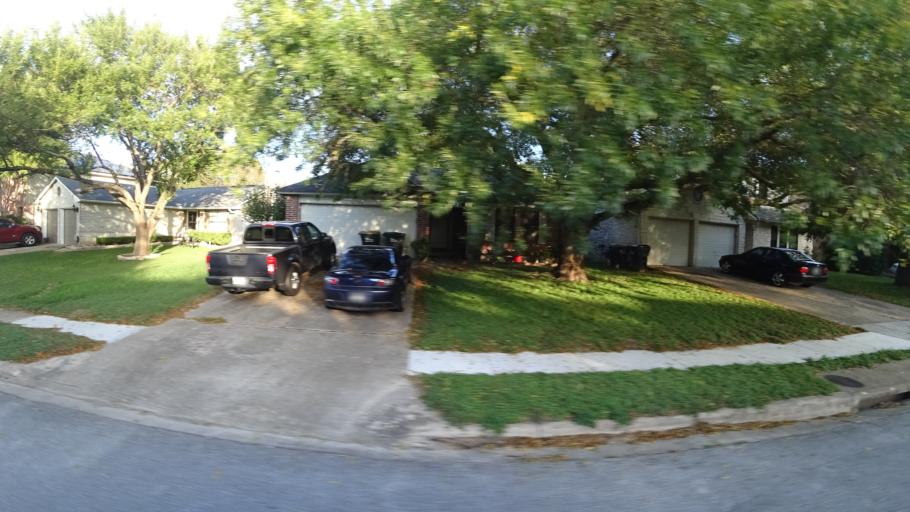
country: US
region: Texas
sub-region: Travis County
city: Pflugerville
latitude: 30.4143
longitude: -97.6496
